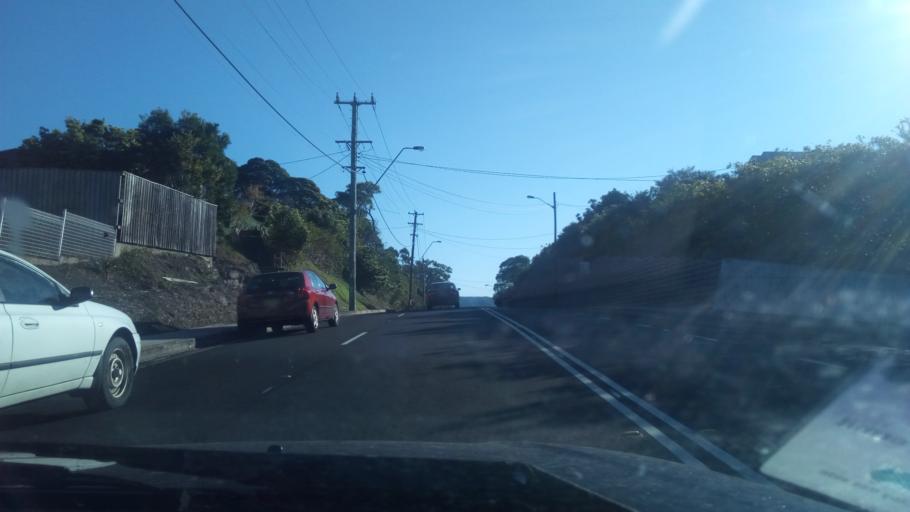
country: AU
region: New South Wales
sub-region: Wollongong
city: Corrimal
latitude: -34.3648
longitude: 150.8987
